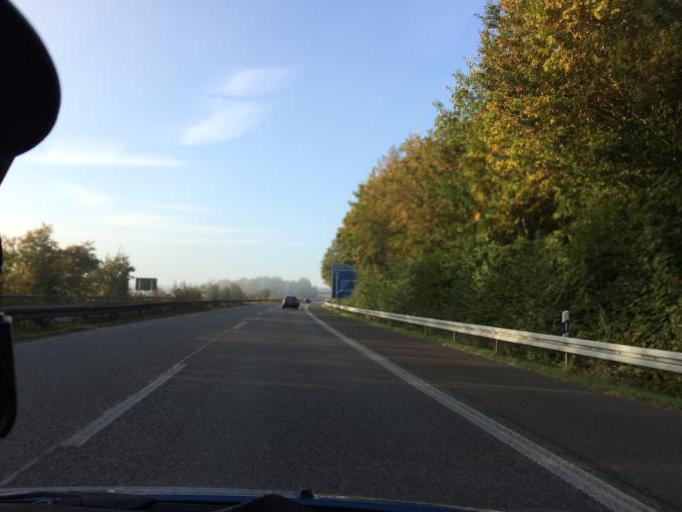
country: DE
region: North Rhine-Westphalia
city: Meckenheim
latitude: 50.6047
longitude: 7.0401
